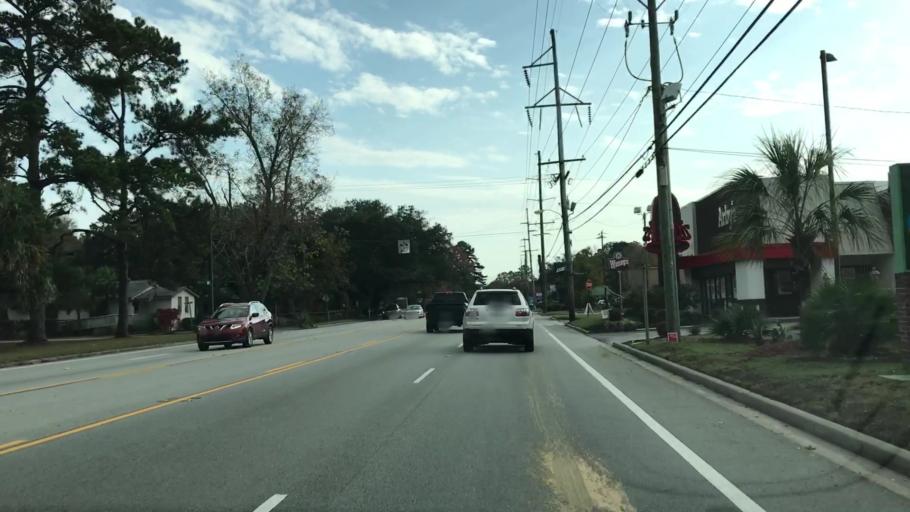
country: US
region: South Carolina
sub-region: Charleston County
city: Charleston
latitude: 32.7587
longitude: -79.9740
